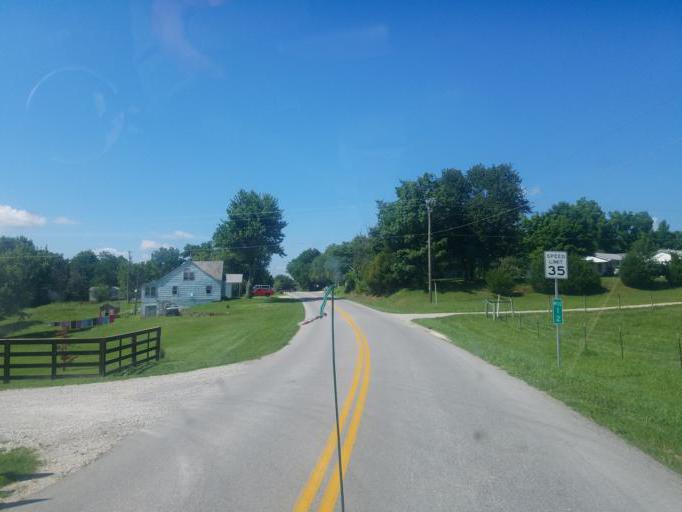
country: US
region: Kentucky
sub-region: Hart County
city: Munfordville
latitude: 37.3032
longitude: -85.9596
